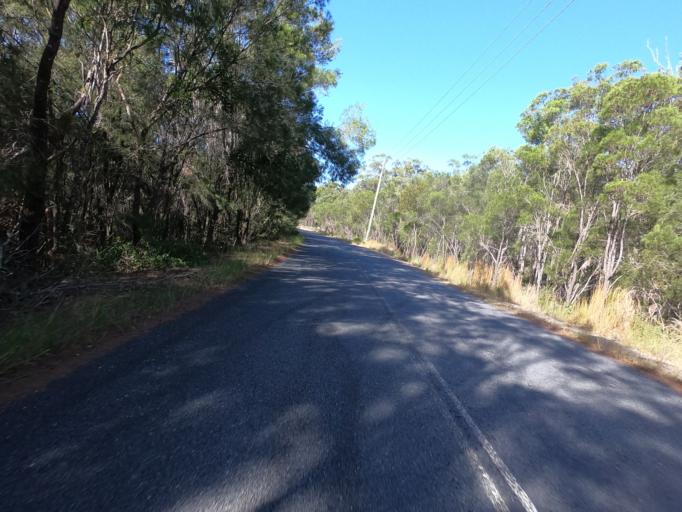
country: AU
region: Queensland
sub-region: Logan
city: Slacks Creek
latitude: -27.6093
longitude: 153.1820
